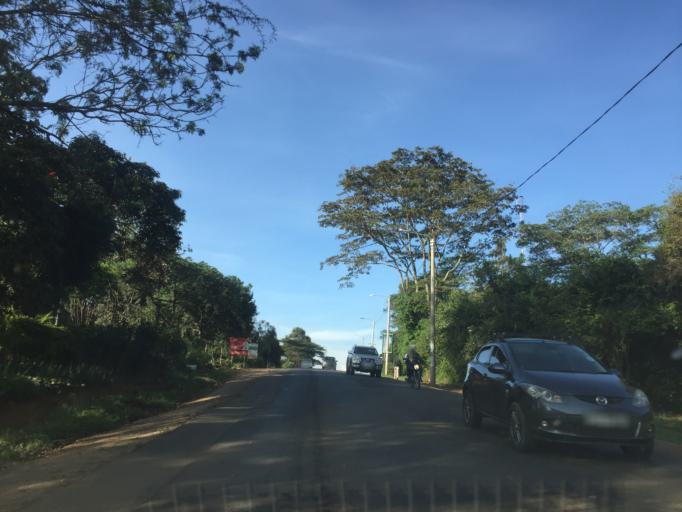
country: KE
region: Nairobi Area
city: Nairobi
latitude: -1.3488
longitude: 36.7647
